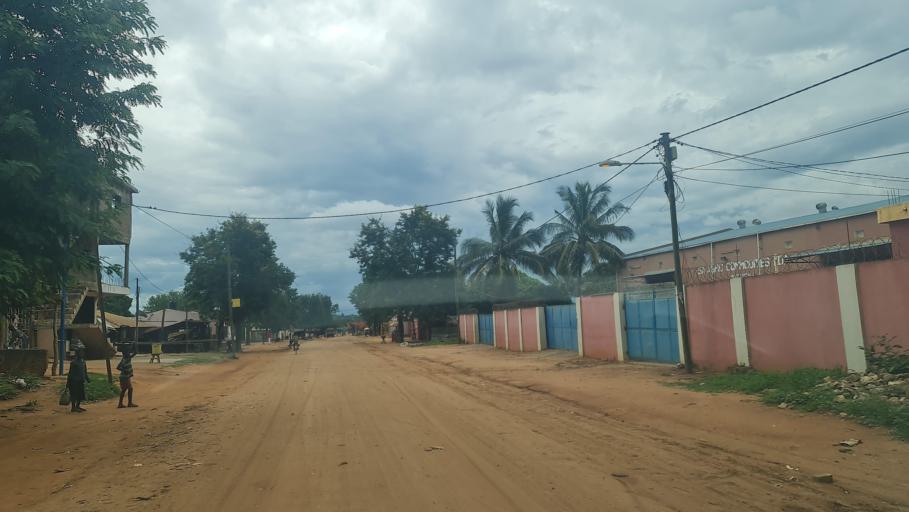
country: MW
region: Southern Region
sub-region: Nsanje District
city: Nsanje
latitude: -17.3295
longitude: 35.5920
